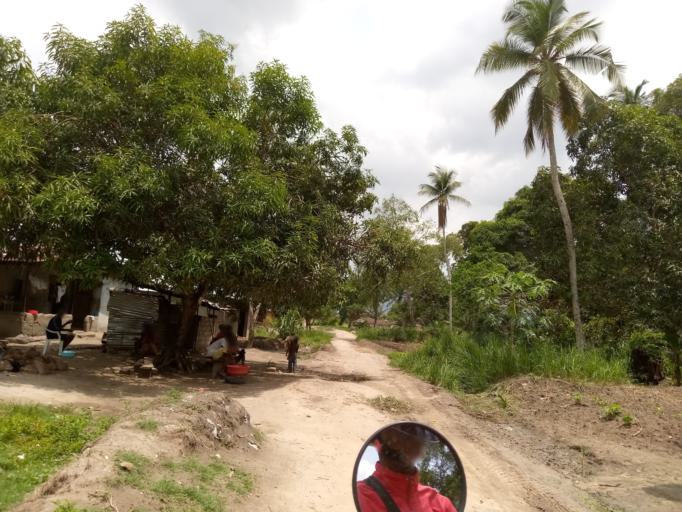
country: SL
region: Western Area
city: Waterloo
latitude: 8.3204
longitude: -13.0332
